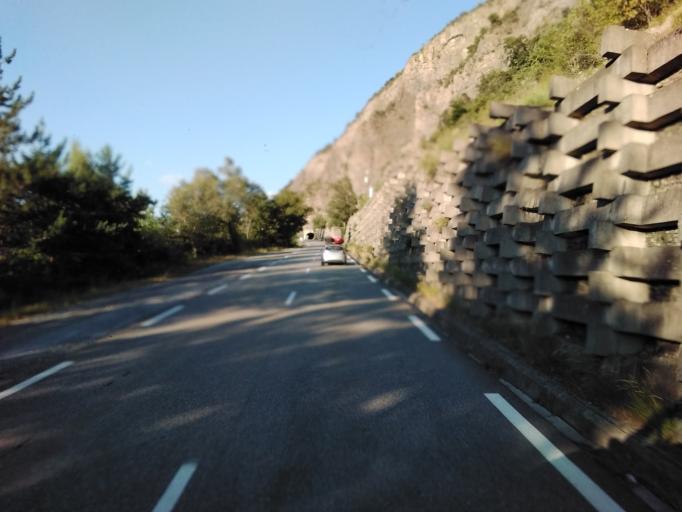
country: FR
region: Provence-Alpes-Cote d'Azur
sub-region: Departement des Hautes-Alpes
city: Chorges
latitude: 44.4594
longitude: 6.2512
